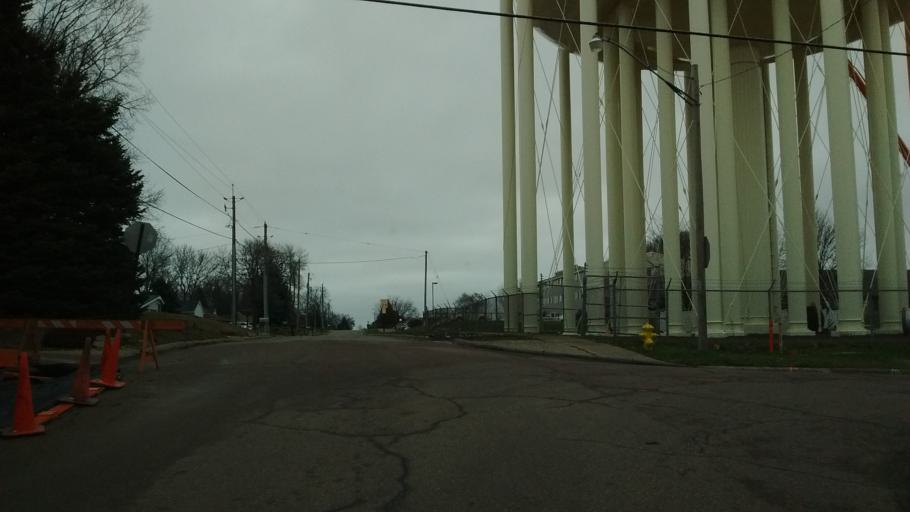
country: US
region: Iowa
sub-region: Woodbury County
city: Sioux City
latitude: 42.4791
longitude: -96.3397
